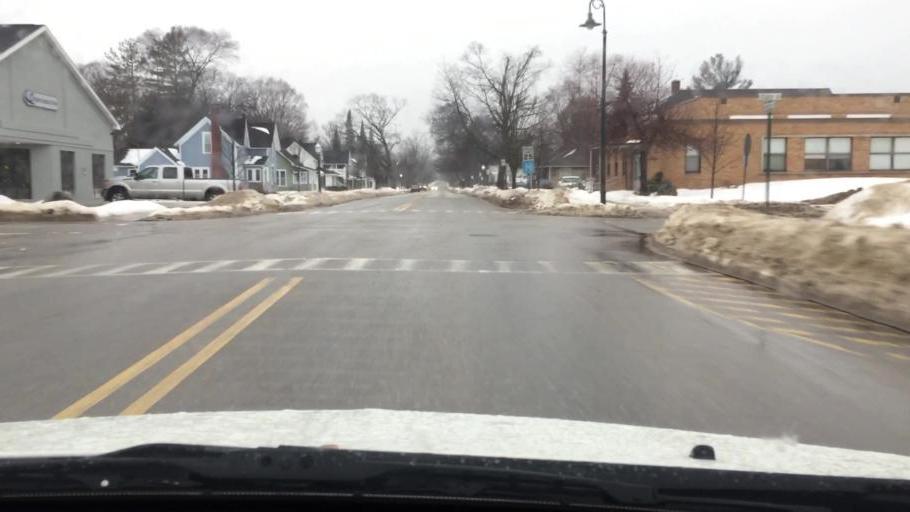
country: US
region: Michigan
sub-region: Charlevoix County
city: Charlevoix
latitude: 45.3152
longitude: -85.2604
